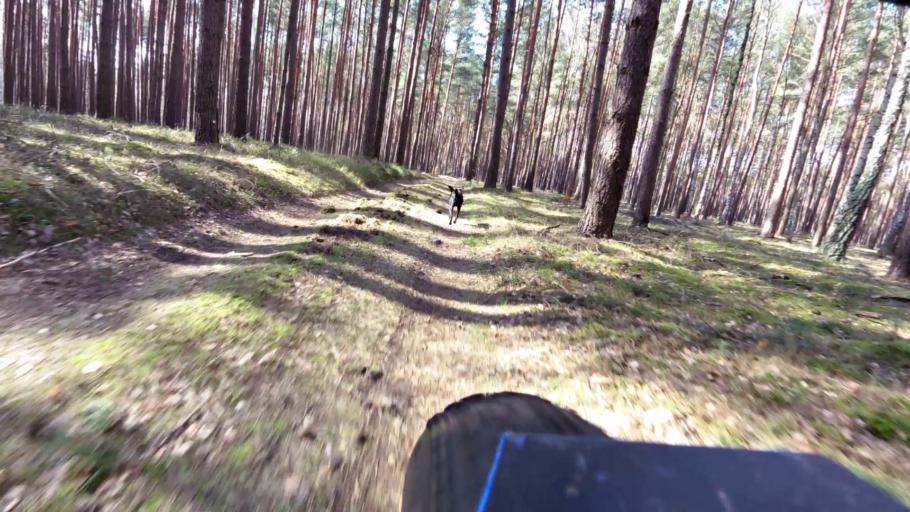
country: PL
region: Lubusz
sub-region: Powiat slubicki
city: Cybinka
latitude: 52.2094
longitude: 14.9022
